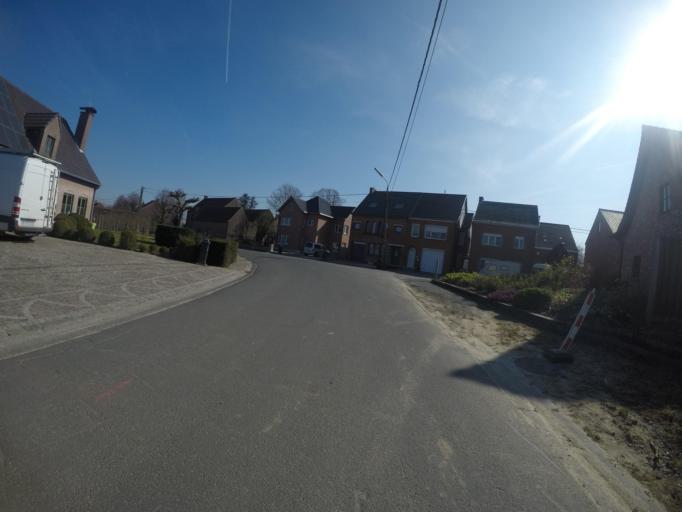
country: BE
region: Flanders
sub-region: Provincie Oost-Vlaanderen
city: Sint-Maria-Lierde
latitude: 50.7824
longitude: 3.8352
